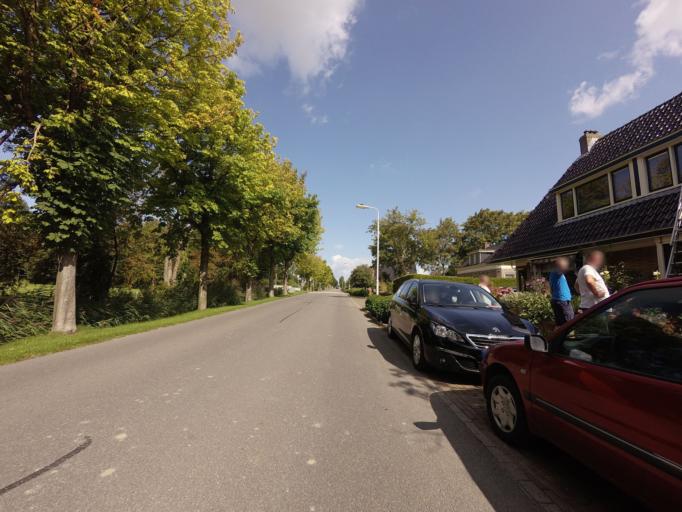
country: NL
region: Friesland
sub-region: Gemeente Het Bildt
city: Sint Annaparochie
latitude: 53.2803
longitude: 5.6563
